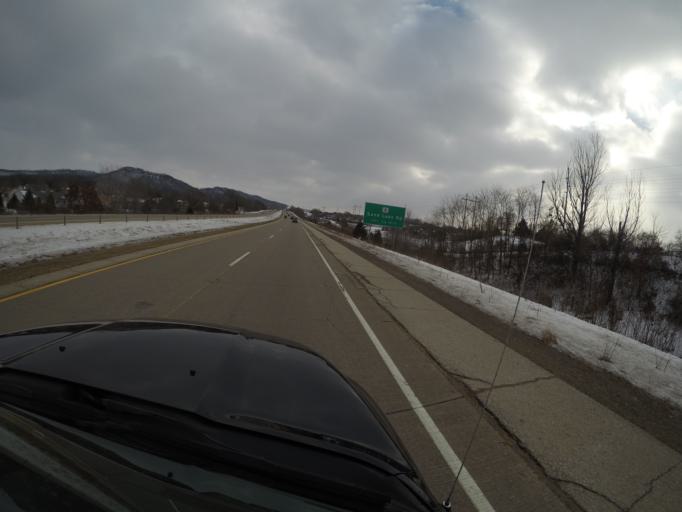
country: US
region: Wisconsin
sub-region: La Crosse County
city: Onalaska
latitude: 43.9111
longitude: -91.2340
